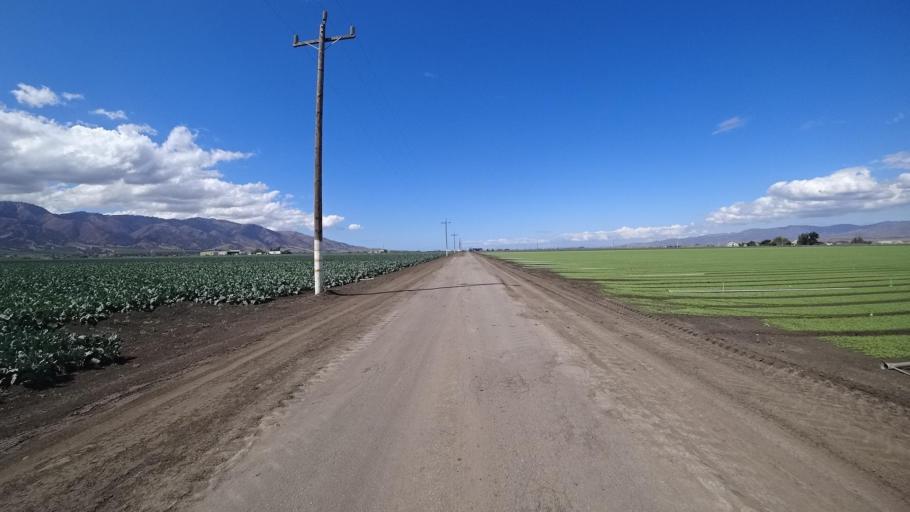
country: US
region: California
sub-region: Monterey County
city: Gonzales
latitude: 36.5130
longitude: -121.4776
